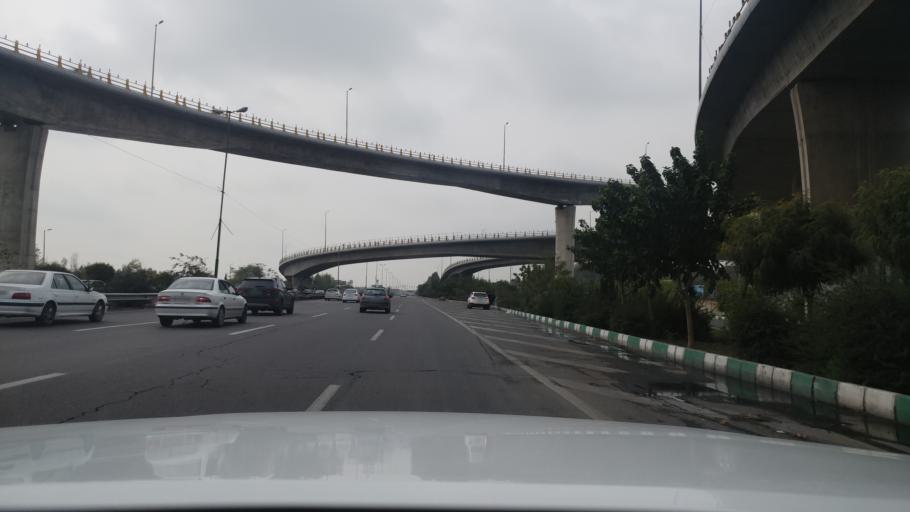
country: IR
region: Tehran
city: Tehran
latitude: 35.7169
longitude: 51.2997
